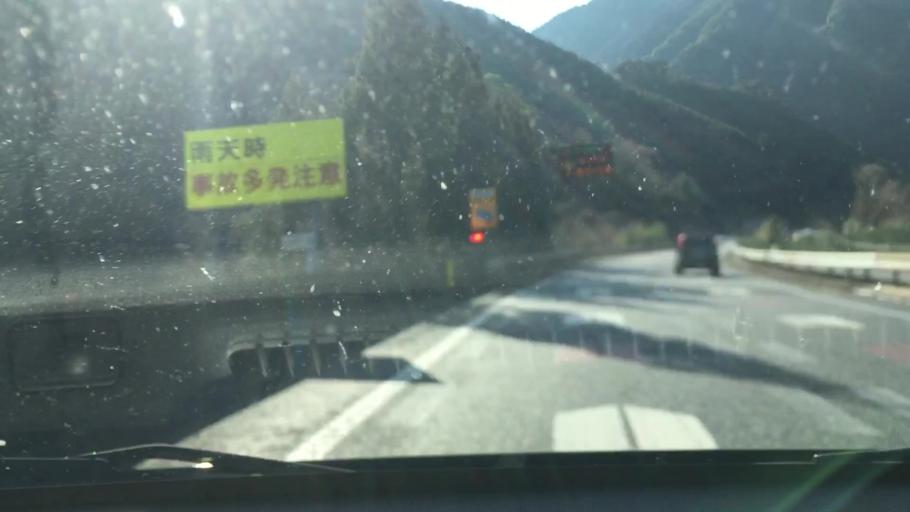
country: JP
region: Kumamoto
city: Hitoyoshi
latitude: 32.3173
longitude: 130.7548
